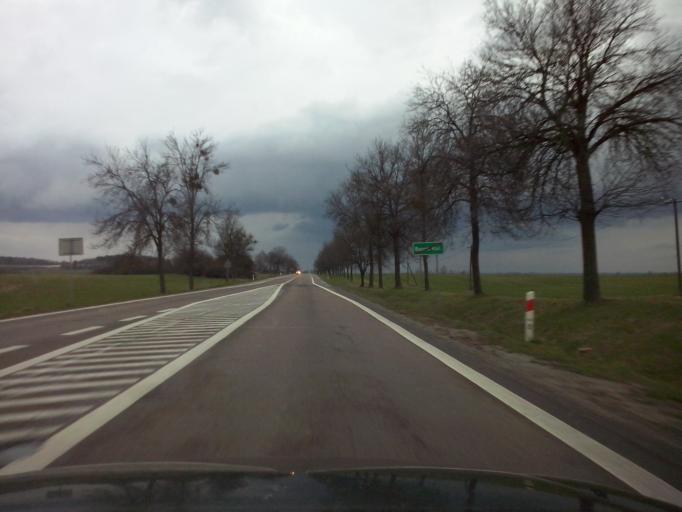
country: PL
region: Lublin Voivodeship
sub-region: Powiat chelmski
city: Rejowiec Fabryczny
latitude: 51.1744
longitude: 23.2651
